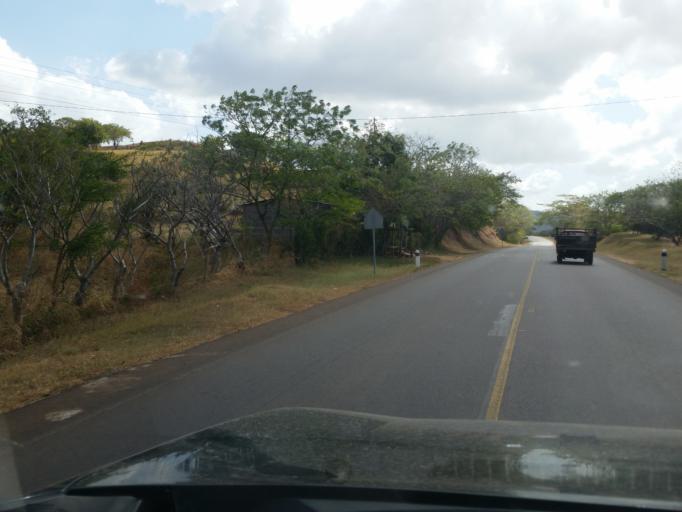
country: NI
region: Chontales
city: Comalapa
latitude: 12.2198
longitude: -85.6383
